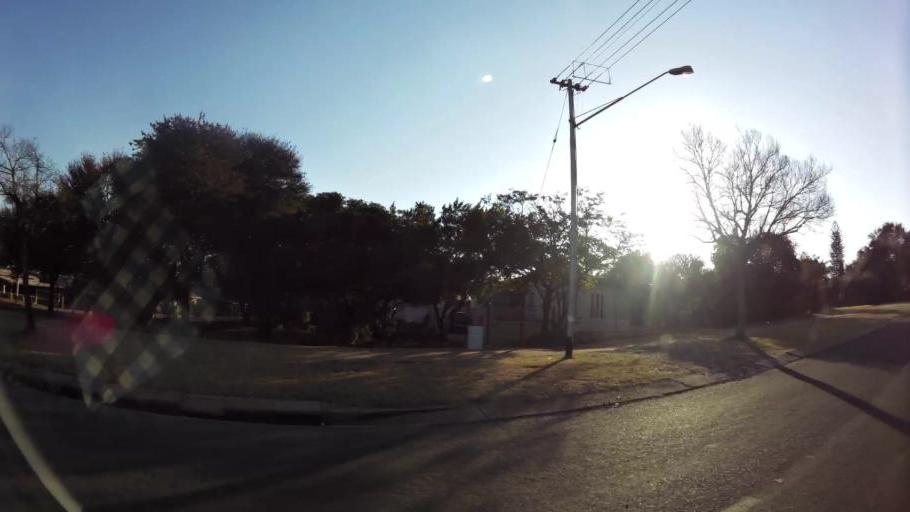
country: ZA
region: Gauteng
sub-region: City of Tshwane Metropolitan Municipality
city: Pretoria
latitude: -25.7372
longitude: 28.1240
